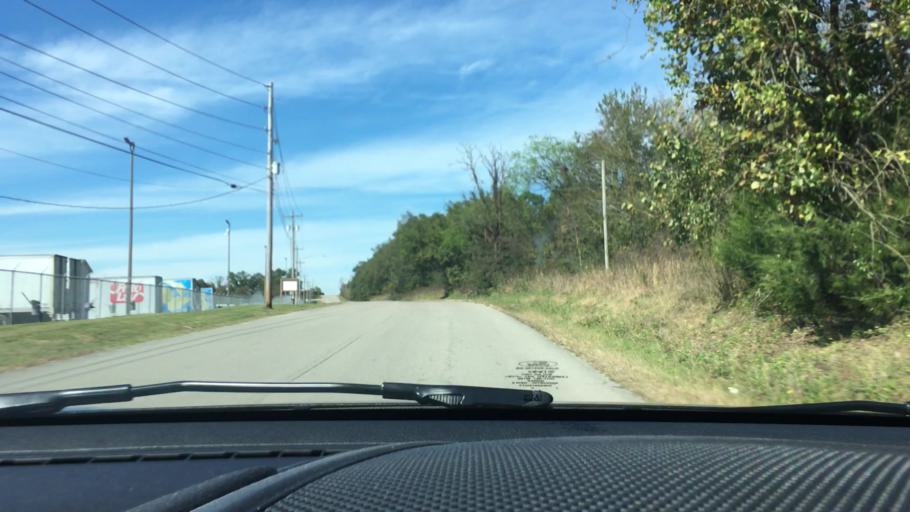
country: US
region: Tennessee
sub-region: Giles County
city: Pulaski
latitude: 35.2182
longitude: -87.0628
